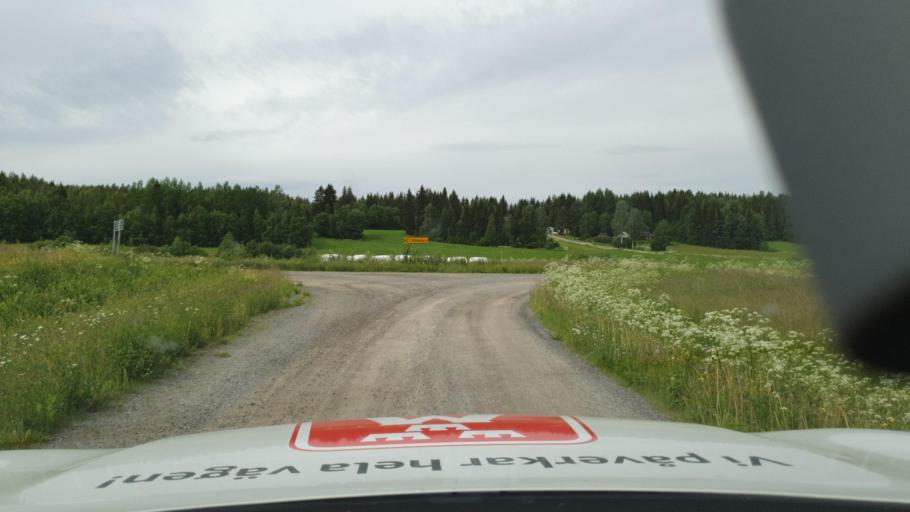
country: SE
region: Vaesterbotten
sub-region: Robertsfors Kommun
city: Robertsfors
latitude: 64.2622
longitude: 20.6319
